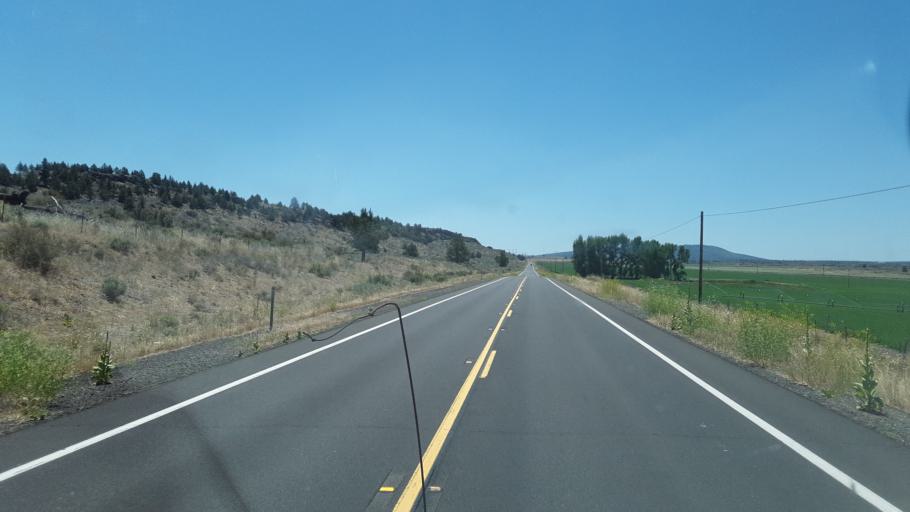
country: US
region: California
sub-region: Siskiyou County
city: Tulelake
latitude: 41.7411
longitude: -121.2999
